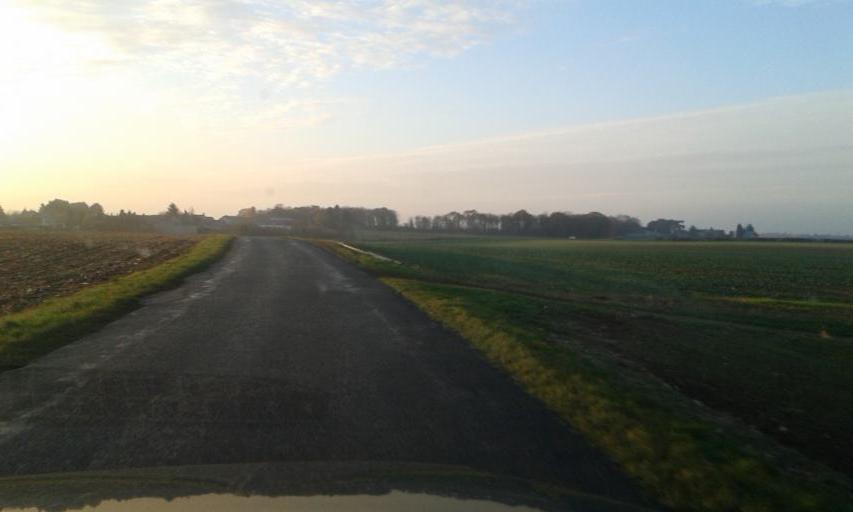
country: FR
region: Centre
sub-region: Departement du Loiret
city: Tavers
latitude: 47.7721
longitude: 1.5551
